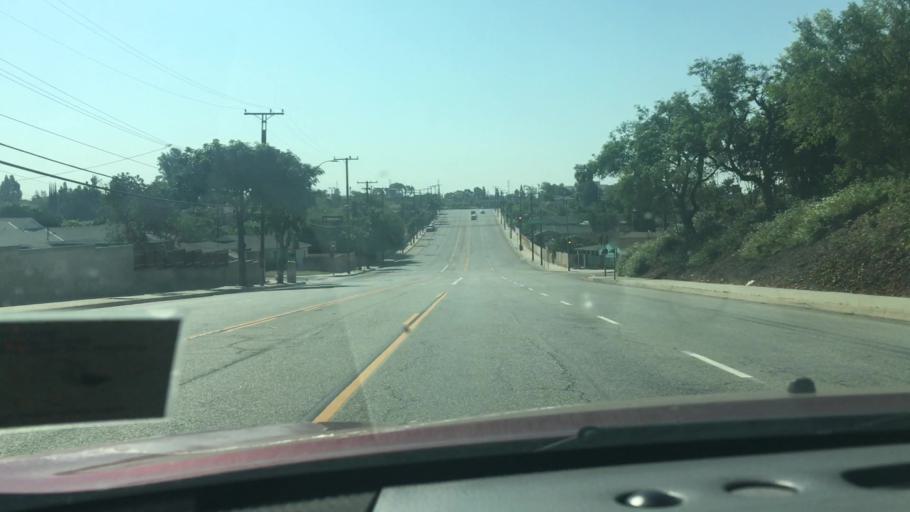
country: US
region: California
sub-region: Los Angeles County
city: La Mirada
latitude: 33.9211
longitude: -118.0184
